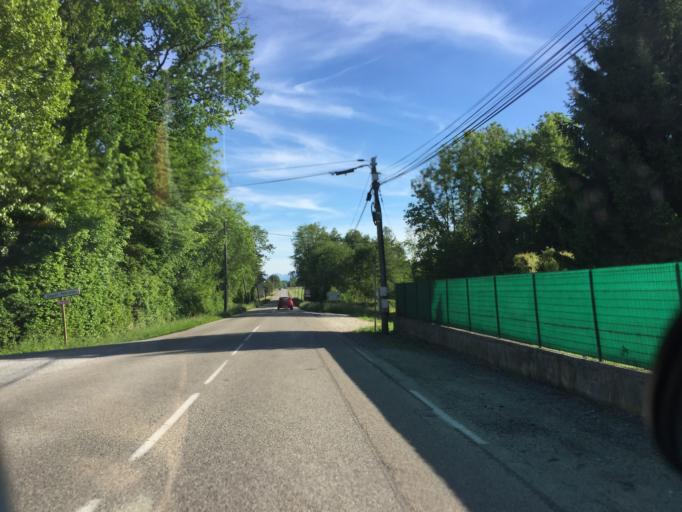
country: FR
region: Rhone-Alpes
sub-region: Departement de la Savoie
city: Albens
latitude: 45.8029
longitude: 5.9497
